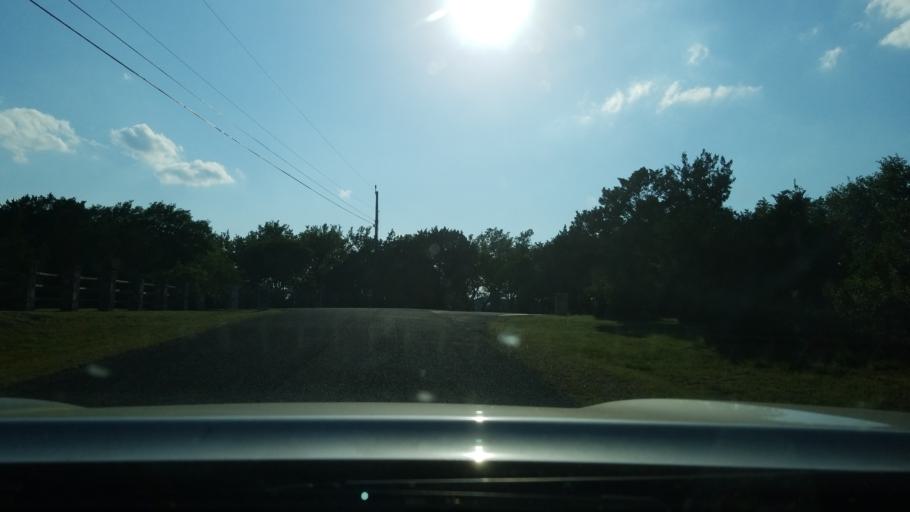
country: US
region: Texas
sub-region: Bexar County
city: Timberwood Park
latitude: 29.7054
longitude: -98.4399
